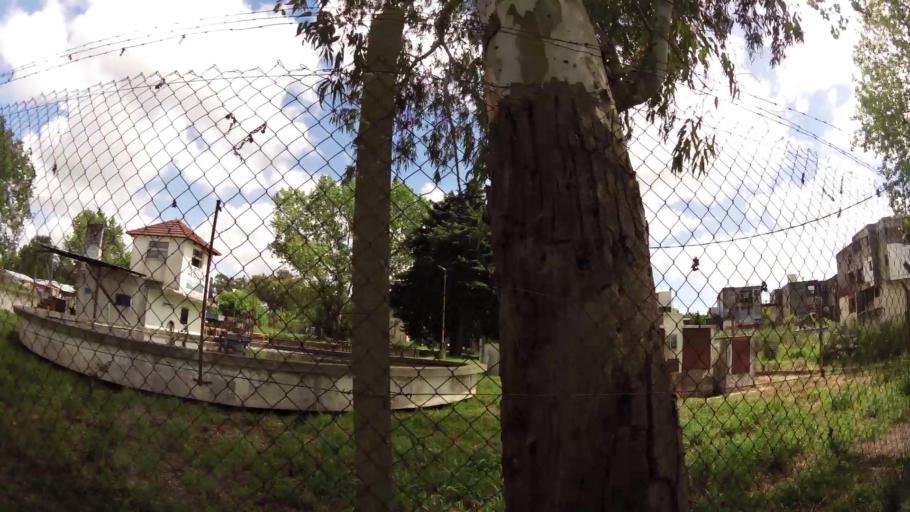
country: AR
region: Buenos Aires
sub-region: Partido de Quilmes
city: Quilmes
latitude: -34.8348
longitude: -58.2216
